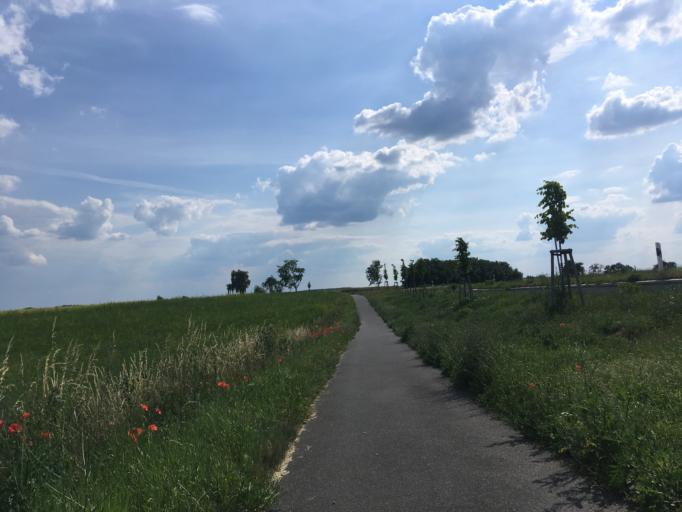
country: DE
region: Brandenburg
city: Steinhofel
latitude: 52.4212
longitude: 14.1078
